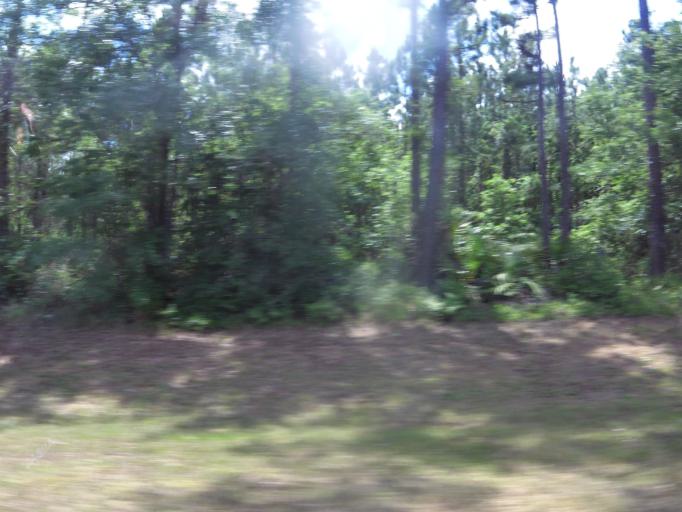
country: US
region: Florida
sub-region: Clay County
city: Green Cove Springs
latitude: 29.9535
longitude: -81.7392
